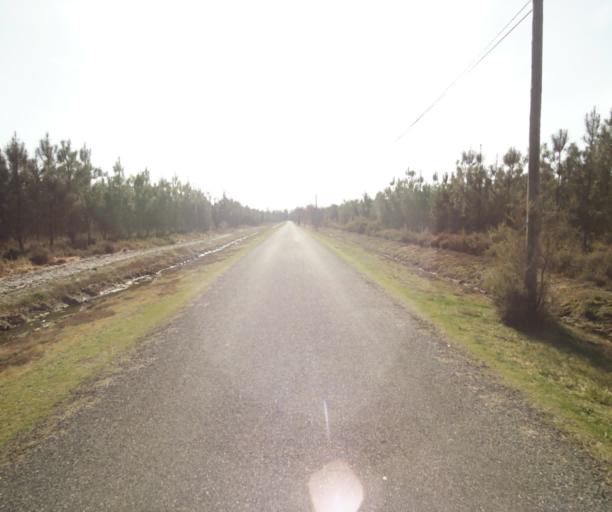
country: FR
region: Aquitaine
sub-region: Departement des Landes
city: Roquefort
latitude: 44.1317
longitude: -0.1896
